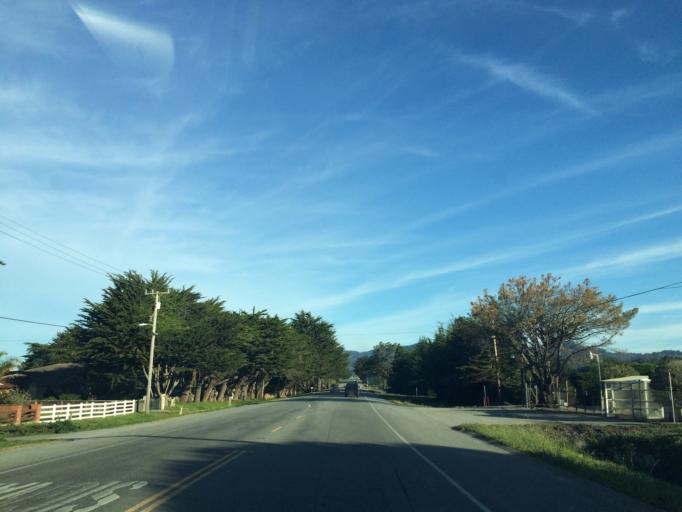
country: US
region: California
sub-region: San Mateo County
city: Half Moon Bay
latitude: 37.4373
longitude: -122.4273
